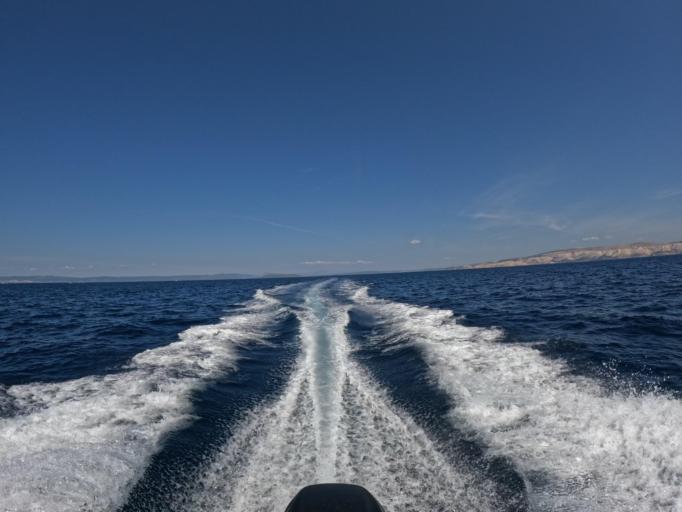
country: HR
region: Primorsko-Goranska
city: Lopar
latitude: 44.8776
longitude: 14.6606
